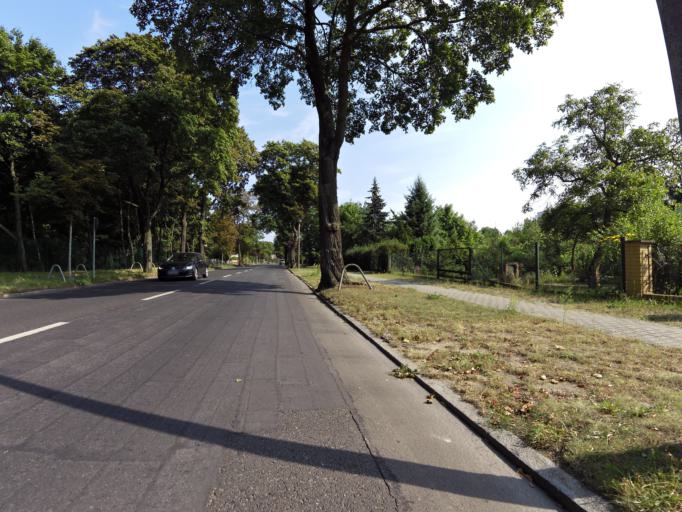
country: DE
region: Berlin
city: Adlershof
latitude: 52.4164
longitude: 13.5567
